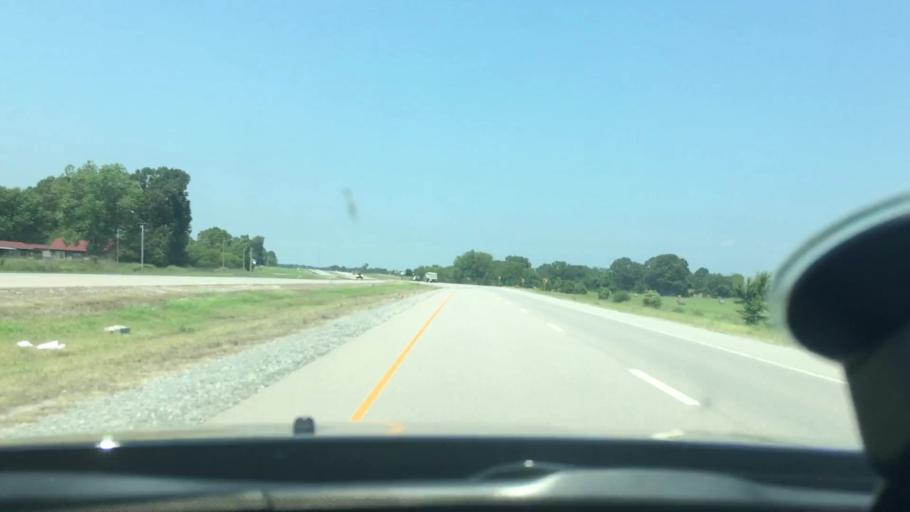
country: US
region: Oklahoma
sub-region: Atoka County
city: Atoka
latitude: 34.3337
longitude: -96.0540
